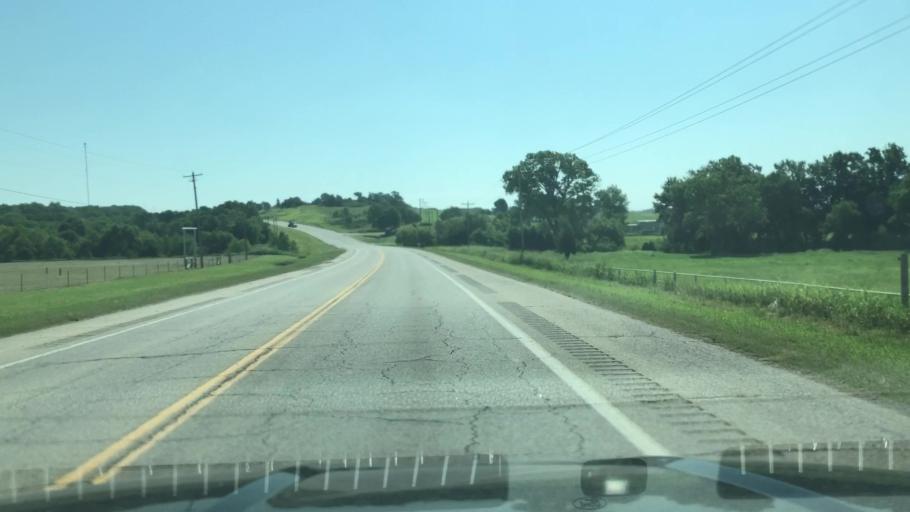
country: US
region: Oklahoma
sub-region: Creek County
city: Drumright
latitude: 35.9884
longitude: -96.5515
